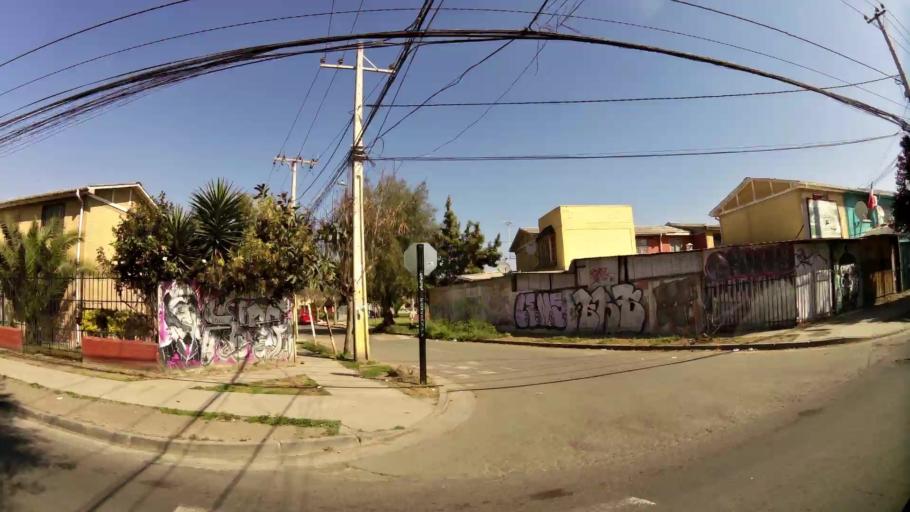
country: CL
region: Santiago Metropolitan
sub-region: Provincia de Santiago
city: Lo Prado
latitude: -33.3547
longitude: -70.7479
